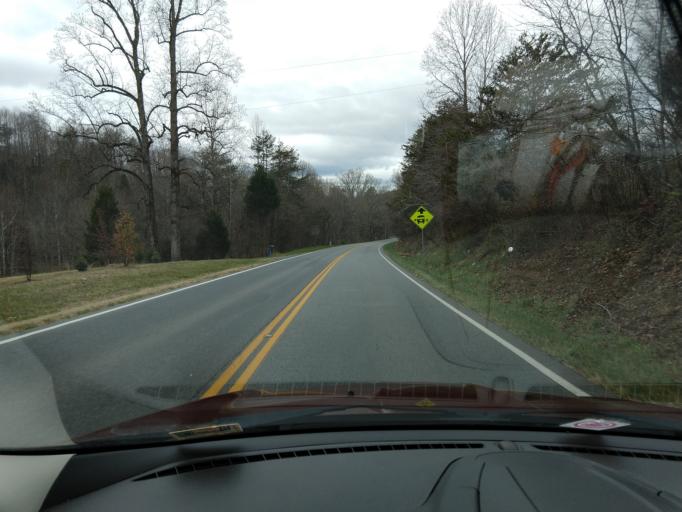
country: US
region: Virginia
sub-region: Botetourt County
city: Blue Ridge
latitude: 37.2604
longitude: -79.7461
